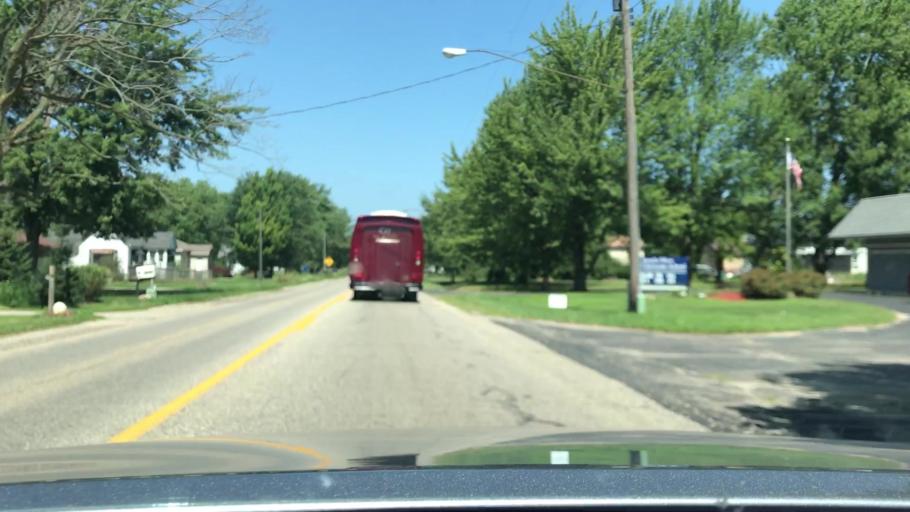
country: US
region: Michigan
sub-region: Ottawa County
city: Zeeland
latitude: 42.8821
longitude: -86.0802
